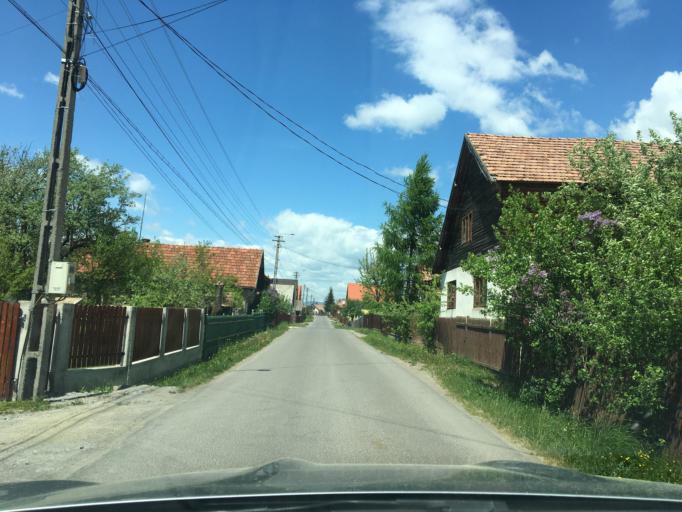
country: RO
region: Harghita
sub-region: Comuna Remetea
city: Remetea
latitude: 46.8012
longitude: 25.4534
